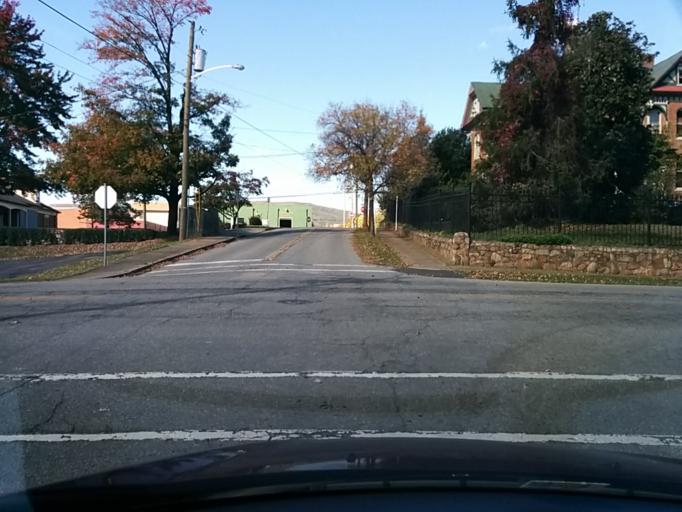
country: US
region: Virginia
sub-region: City of Salem
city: Salem
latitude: 37.2917
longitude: -80.0553
